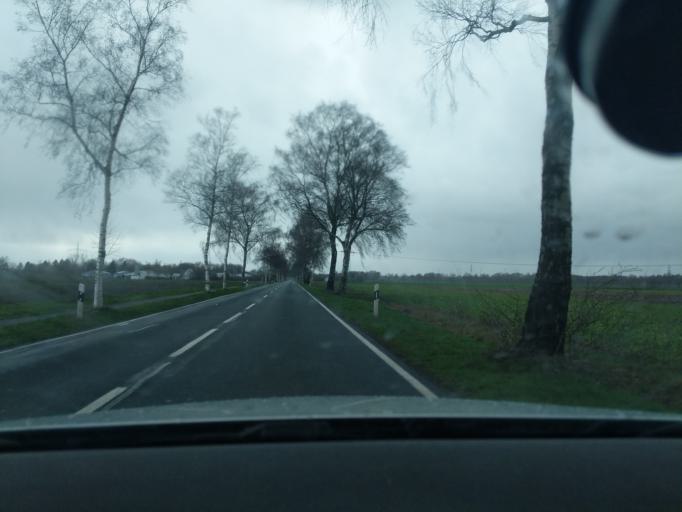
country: DE
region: Lower Saxony
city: Bargstedt
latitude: 53.4618
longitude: 9.4353
